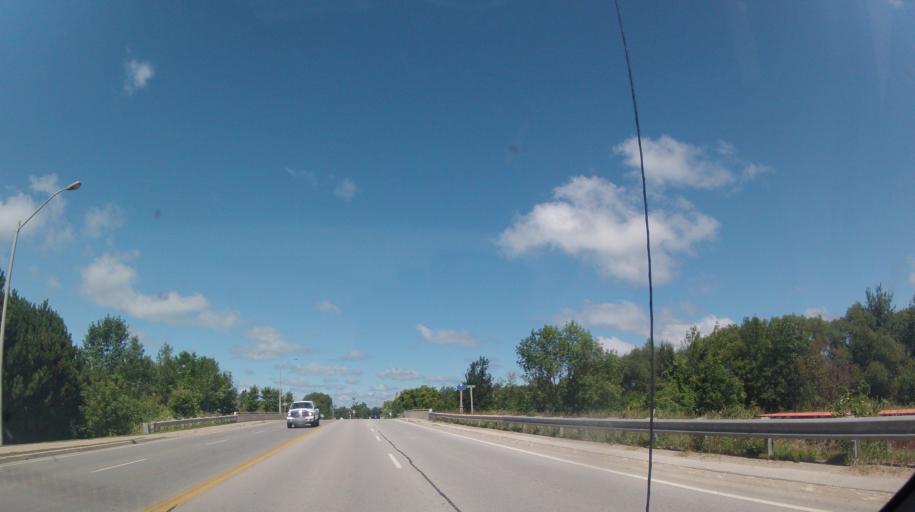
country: CA
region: Ontario
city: Collingwood
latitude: 44.5024
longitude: -80.1972
